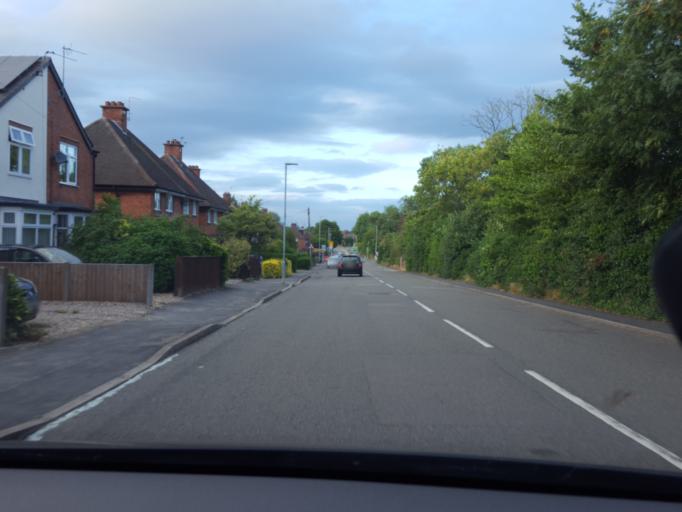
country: GB
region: England
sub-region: Leicestershire
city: Loughborough
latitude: 52.7585
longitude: -1.2164
